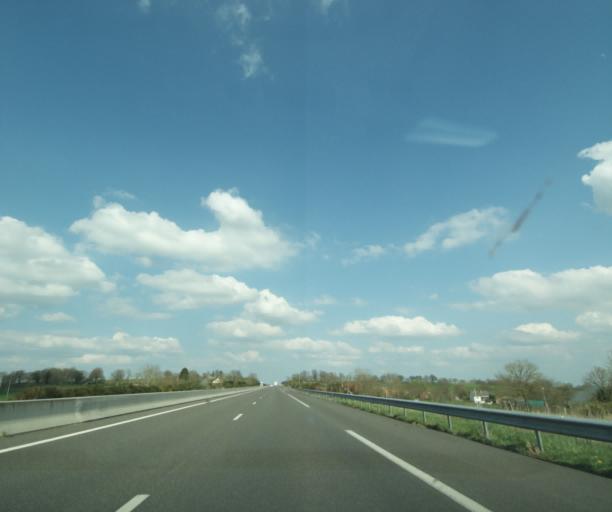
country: FR
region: Auvergne
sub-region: Departement de l'Allier
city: Souvigny
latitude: 46.4253
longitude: 3.1212
